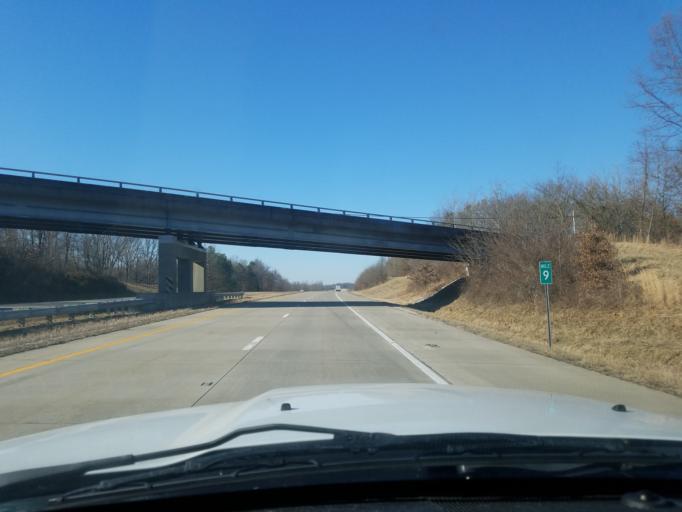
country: US
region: Indiana
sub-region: Warrick County
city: Newburgh
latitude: 37.7596
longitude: -87.4151
